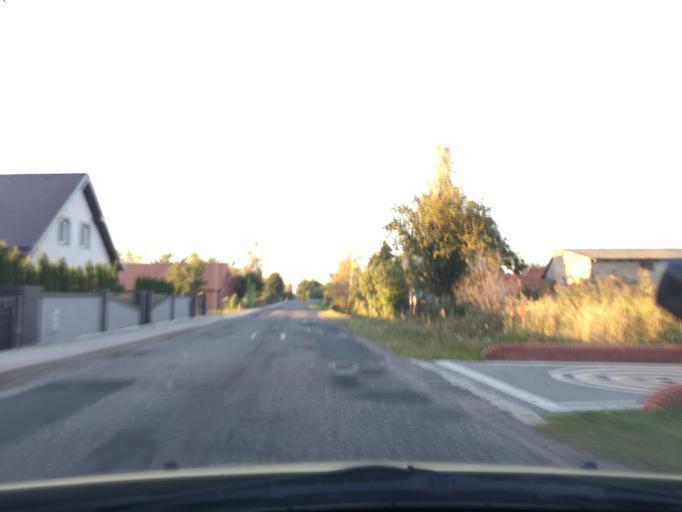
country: PL
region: Greater Poland Voivodeship
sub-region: Powiat pleszewski
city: Dobrzyca
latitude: 51.8117
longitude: 17.6226
